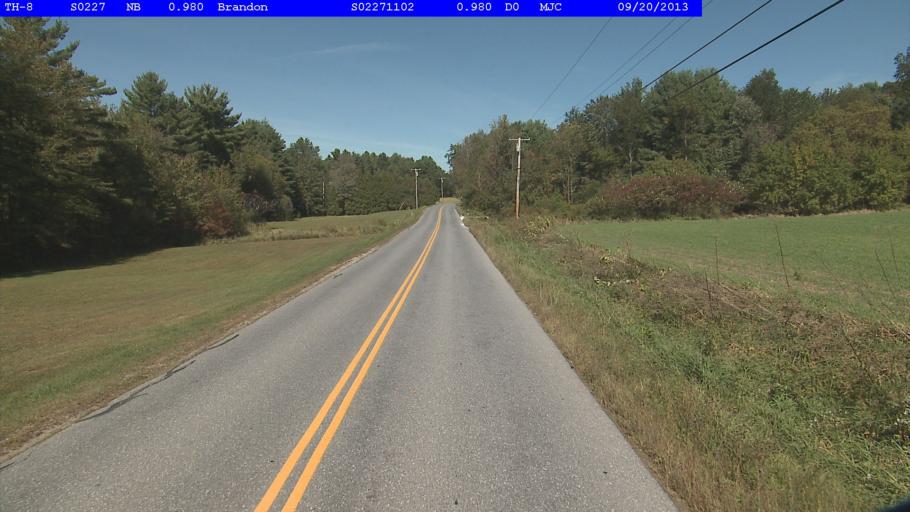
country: US
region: Vermont
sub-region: Rutland County
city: Brandon
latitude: 43.7885
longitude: -73.0537
